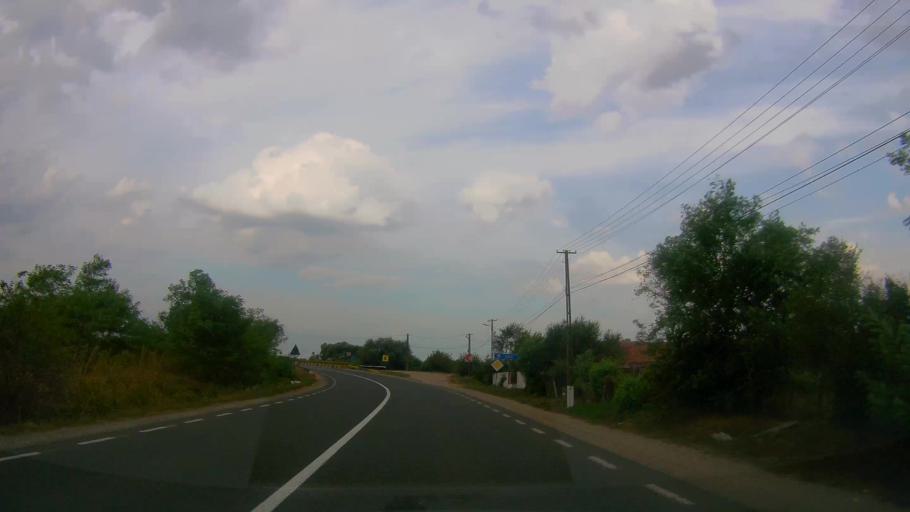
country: RO
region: Satu Mare
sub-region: Comuna Acas
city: Acas
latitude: 47.5415
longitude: 22.7893
